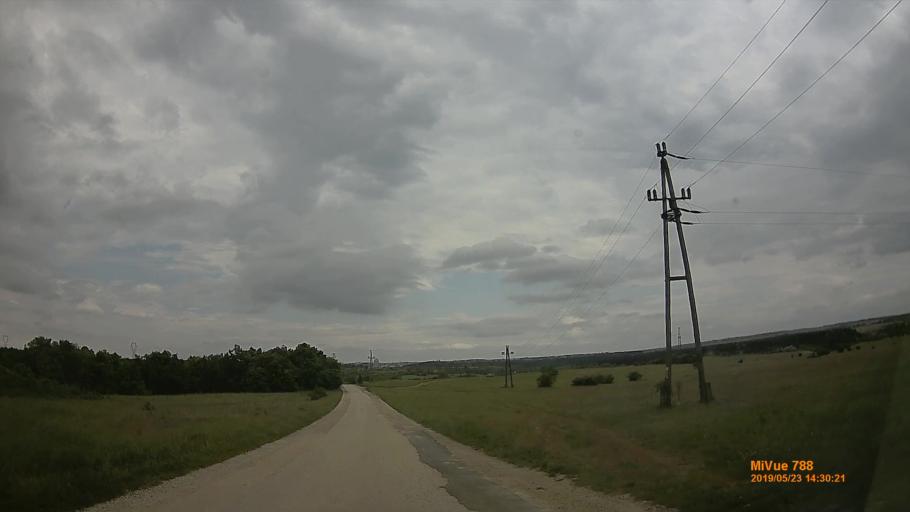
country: HU
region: Veszprem
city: Nemesvamos
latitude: 47.1061
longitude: 17.8560
